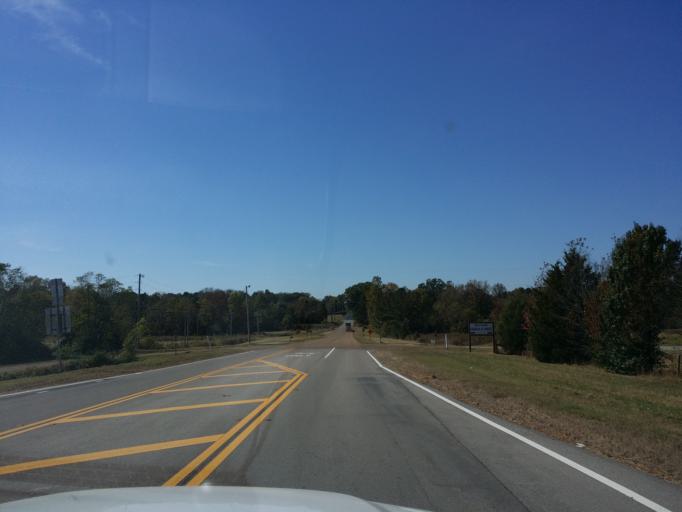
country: US
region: Mississippi
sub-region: Alcorn County
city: Corinth
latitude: 34.9819
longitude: -88.5235
